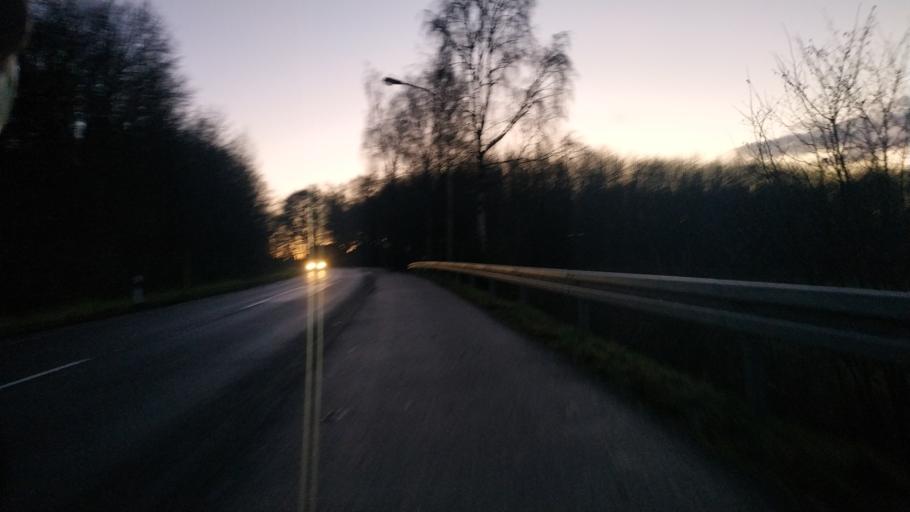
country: DE
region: North Rhine-Westphalia
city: Ibbenburen
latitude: 52.2927
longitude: 7.7355
